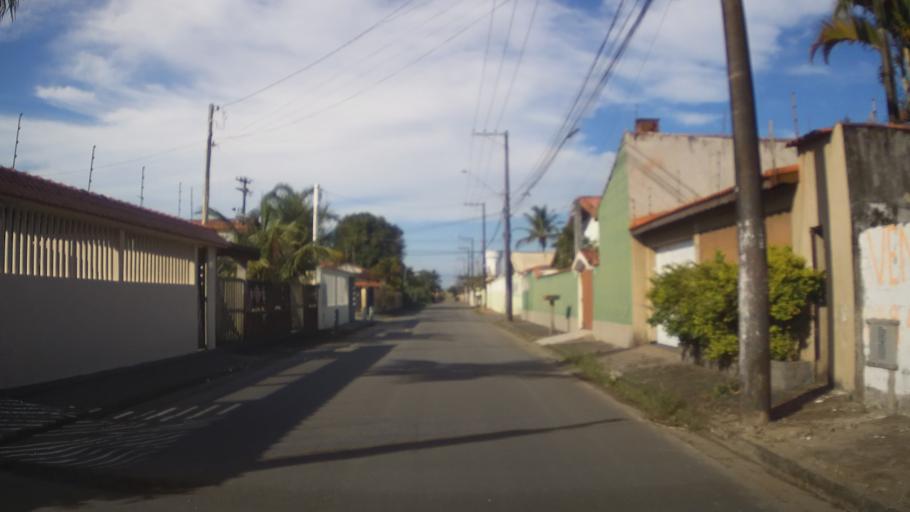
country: BR
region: Sao Paulo
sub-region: Itanhaem
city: Itanhaem
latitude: -24.1594
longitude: -46.7424
